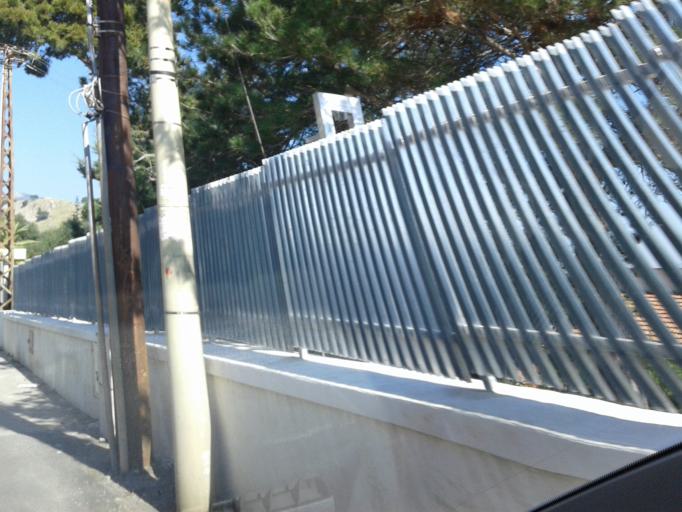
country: IT
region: Sicily
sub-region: Palermo
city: Piano dei Geli
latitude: 38.1127
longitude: 13.2975
